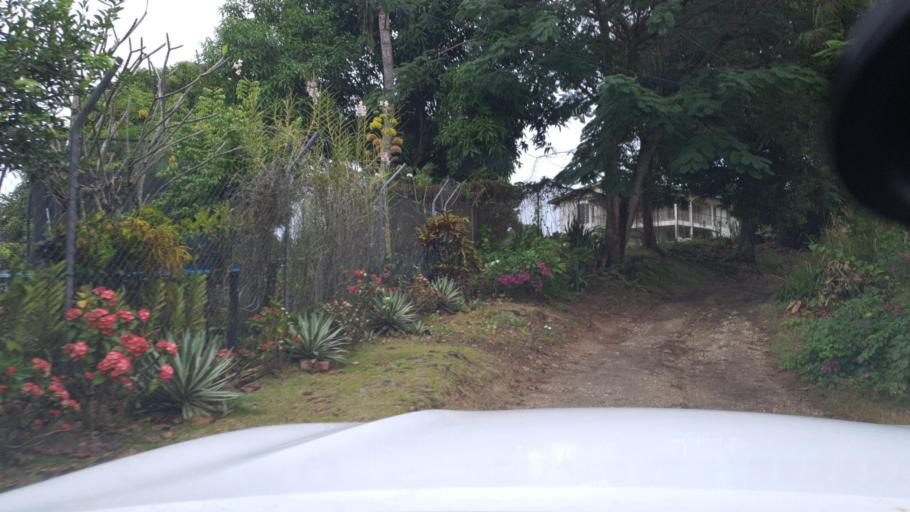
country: SB
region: Guadalcanal
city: Honiara
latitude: -9.4400
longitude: 159.9684
